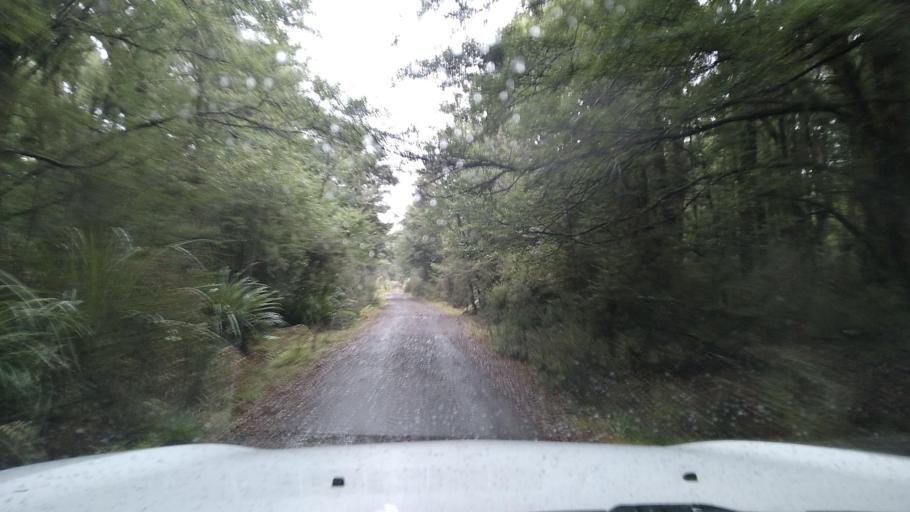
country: NZ
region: Manawatu-Wanganui
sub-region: Ruapehu District
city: Waiouru
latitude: -39.4124
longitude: 175.4954
